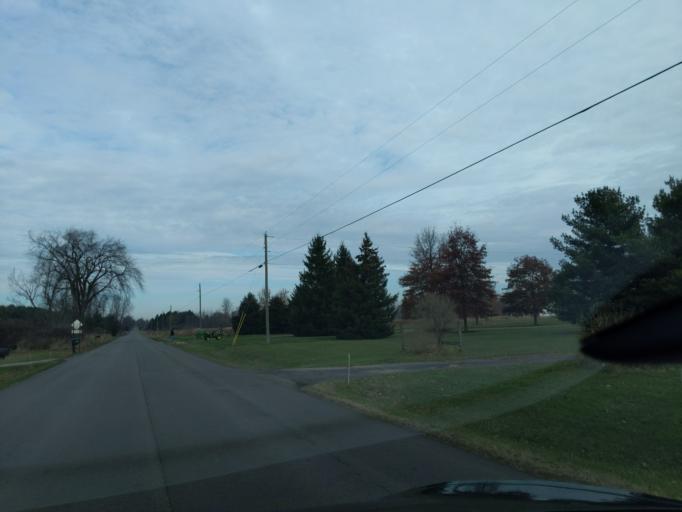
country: US
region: Michigan
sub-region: Ingham County
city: Mason
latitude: 42.5105
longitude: -84.5025
